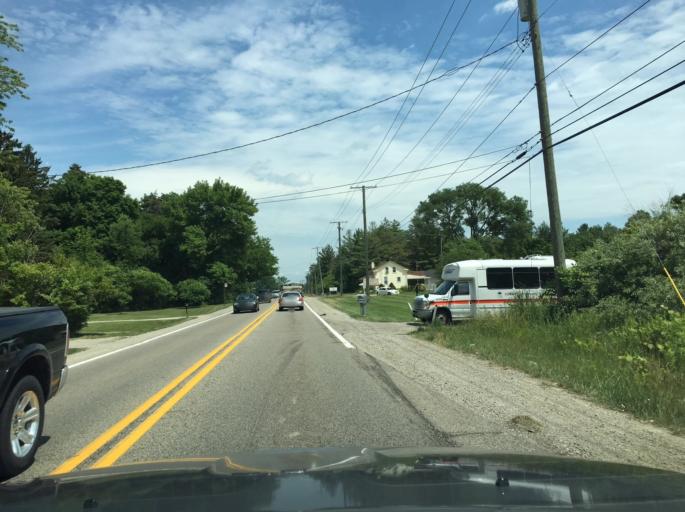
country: US
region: Michigan
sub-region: Macomb County
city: Shelby
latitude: 42.7146
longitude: -83.0031
